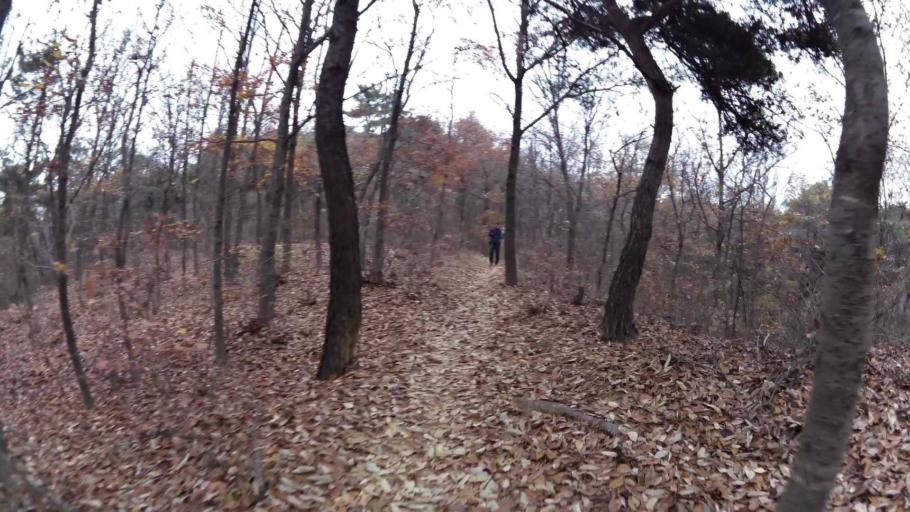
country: KR
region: Daegu
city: Daegu
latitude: 35.8617
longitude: 128.6617
